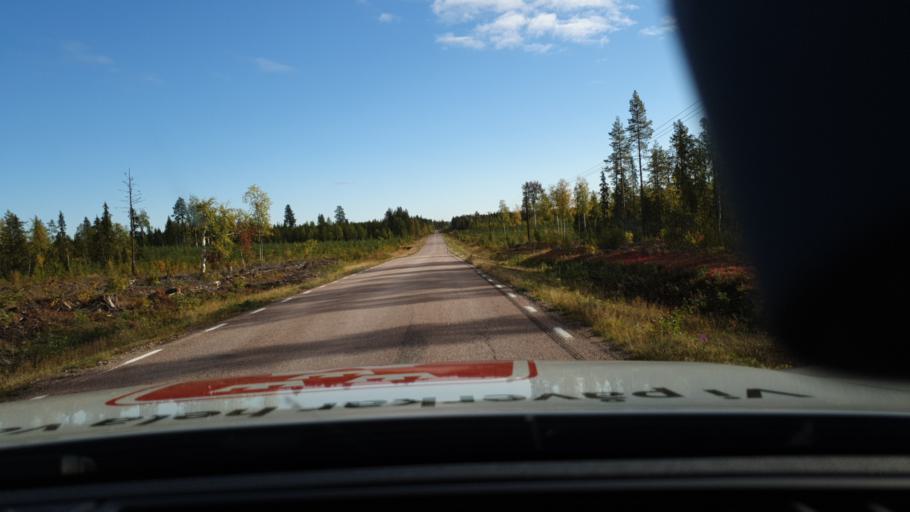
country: SE
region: Norrbotten
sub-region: Pajala Kommun
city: Pajala
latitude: 67.1901
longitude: 23.3050
